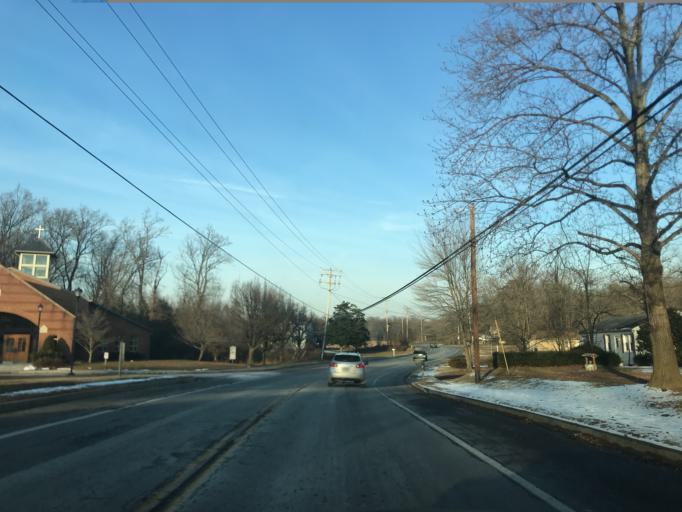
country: US
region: Maryland
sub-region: Harford County
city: Edgewood
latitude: 39.4269
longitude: -76.2845
